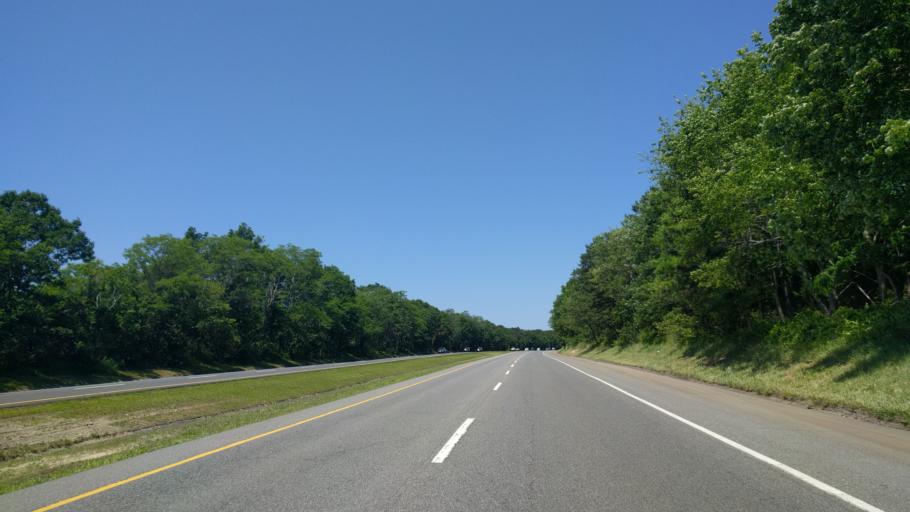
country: US
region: New York
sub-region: Suffolk County
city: Eastport
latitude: 40.8505
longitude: -72.7455
